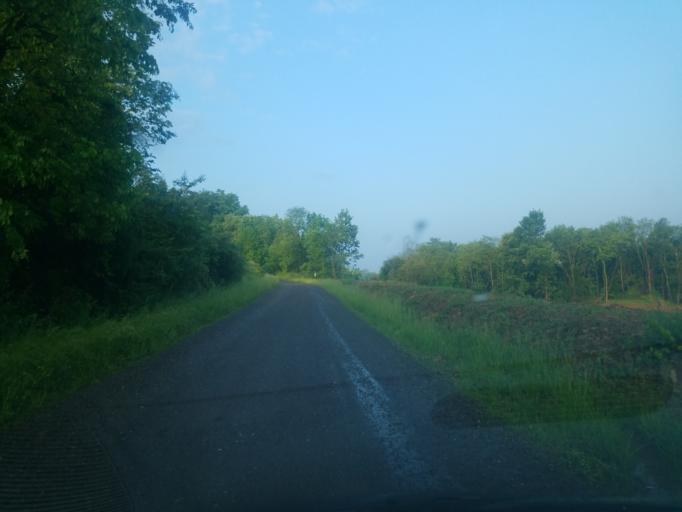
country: US
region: Ohio
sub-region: Stark County
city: Minerva
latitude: 40.7320
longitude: -80.9838
